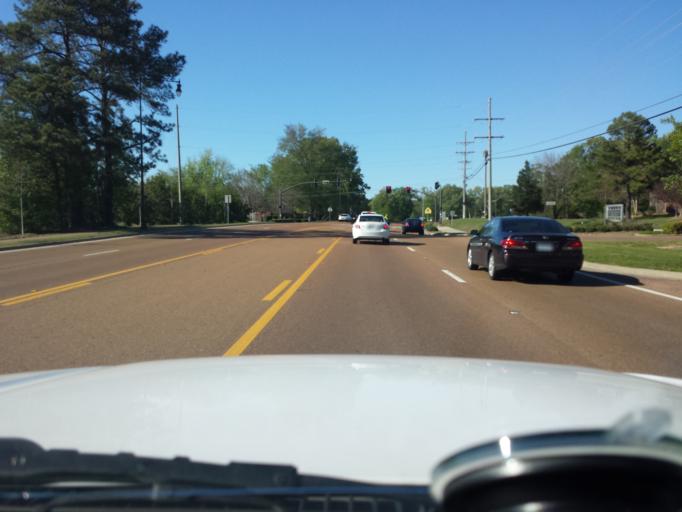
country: US
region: Mississippi
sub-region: Rankin County
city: Flowood
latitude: 32.3478
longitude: -90.0647
